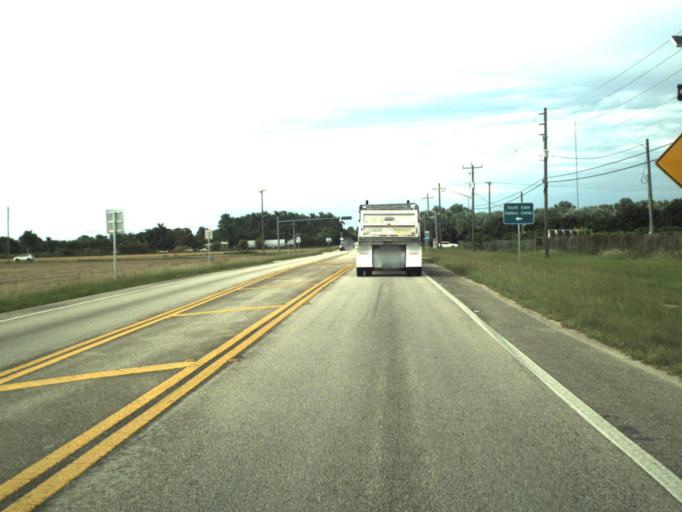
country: US
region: Florida
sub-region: Miami-Dade County
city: Homestead
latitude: 25.4972
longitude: -80.4776
